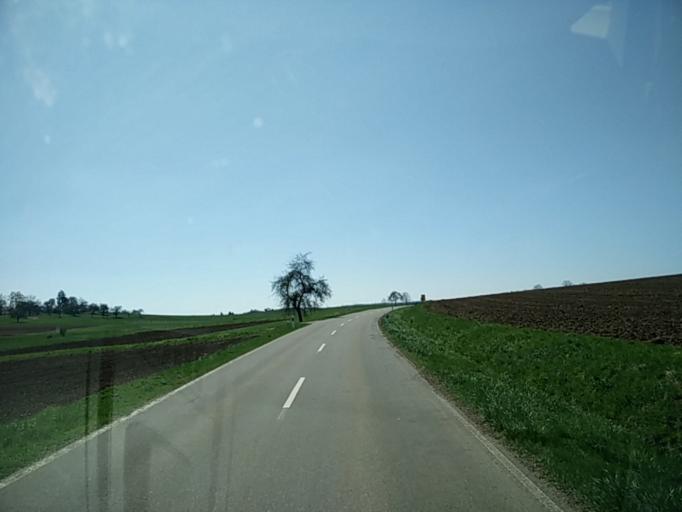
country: DE
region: Baden-Wuerttemberg
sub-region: Tuebingen Region
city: Dusslingen
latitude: 48.4589
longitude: 9.0691
